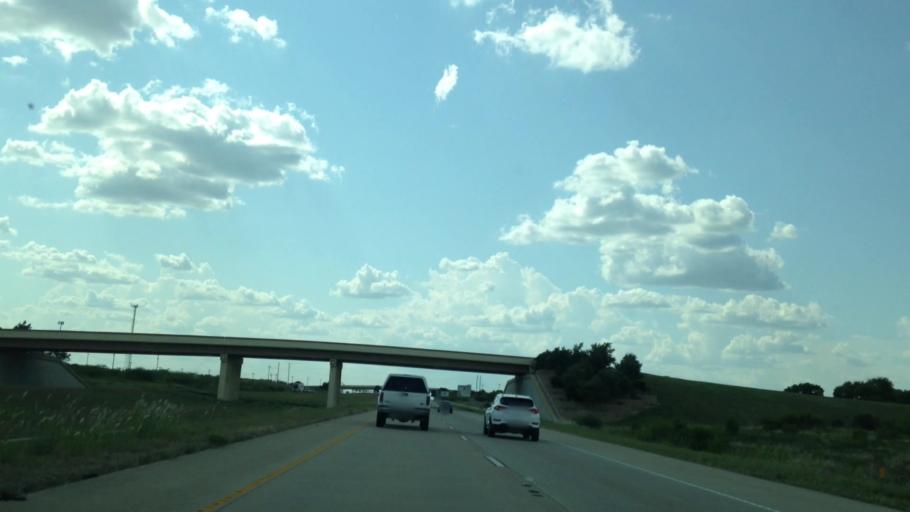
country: US
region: Texas
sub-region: Travis County
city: Onion Creek
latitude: 30.0923
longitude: -97.7546
